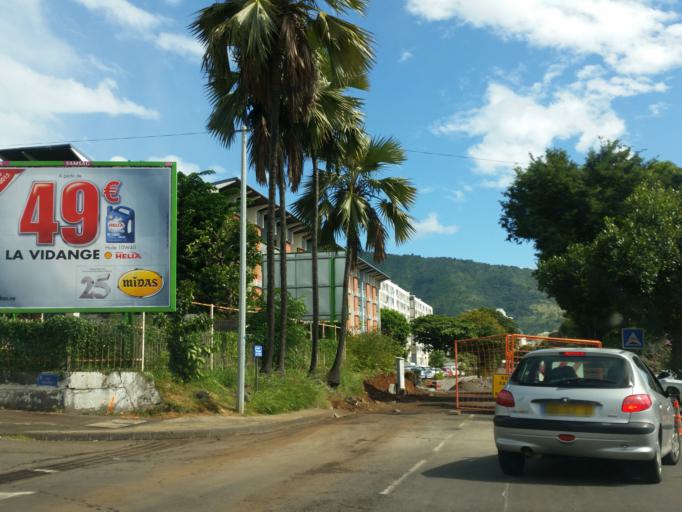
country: RE
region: Reunion
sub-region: Reunion
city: Saint-Denis
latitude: -20.8927
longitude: 55.4640
